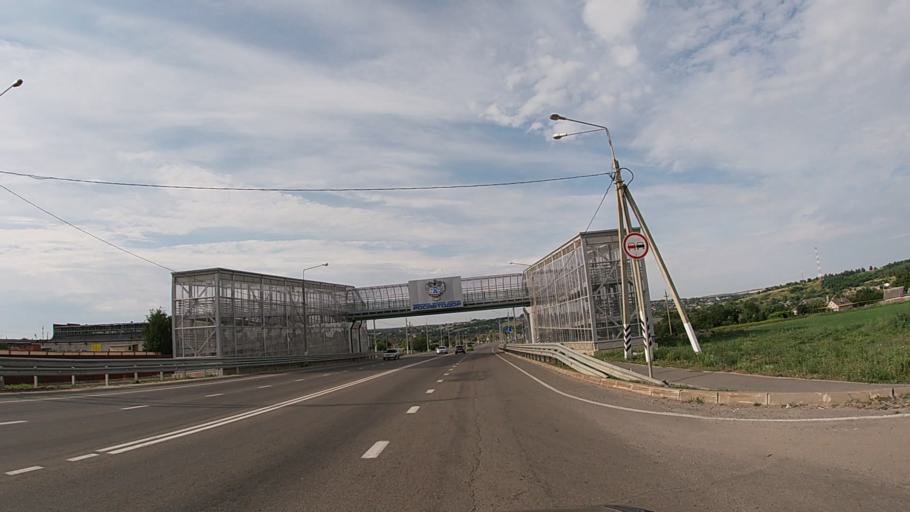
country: RU
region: Belgorod
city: Severnyy
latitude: 50.6412
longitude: 36.4686
